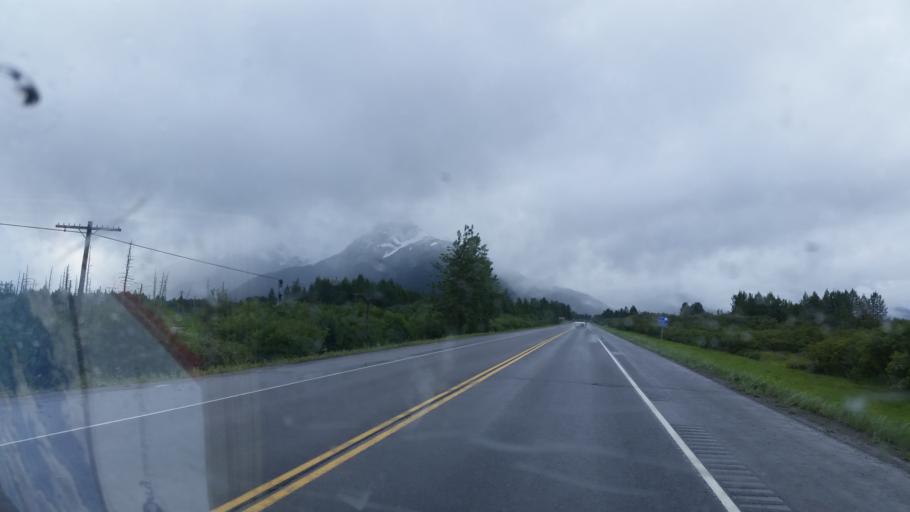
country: US
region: Alaska
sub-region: Anchorage Municipality
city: Girdwood
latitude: 60.8329
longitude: -148.9800
